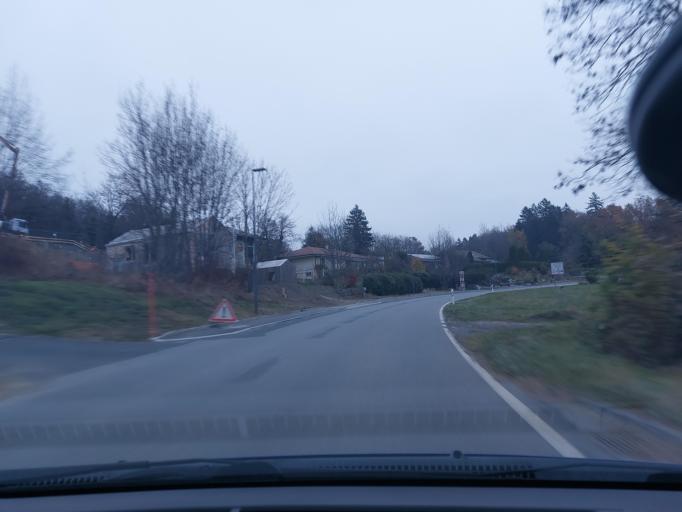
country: CH
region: Valais
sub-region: Sion District
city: Grimisuat
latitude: 46.2626
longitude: 7.3839
